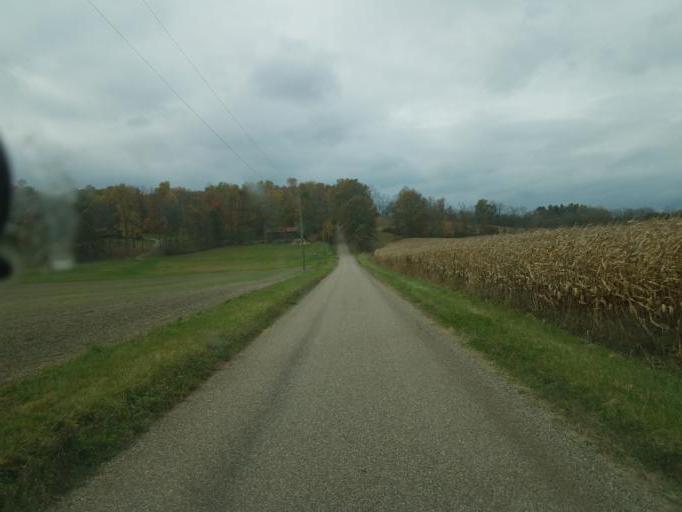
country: US
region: Ohio
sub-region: Ashland County
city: Loudonville
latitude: 40.6245
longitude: -82.1300
